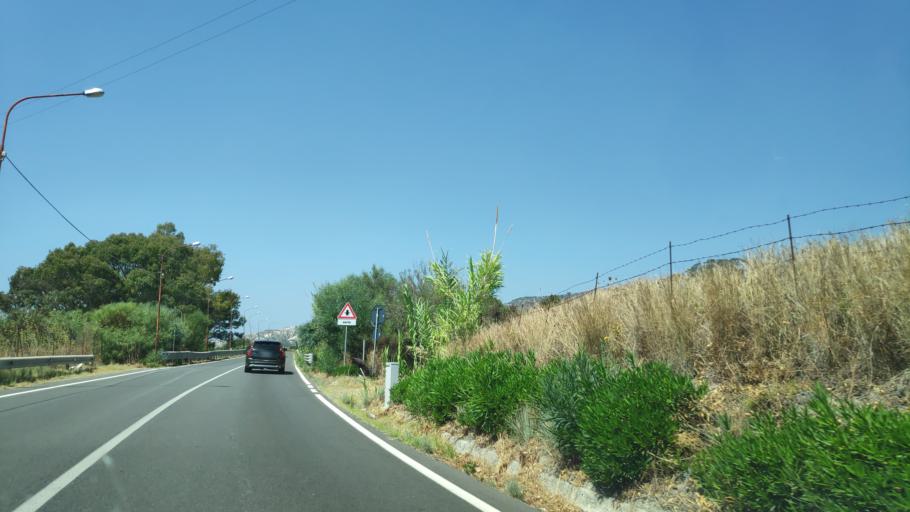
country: IT
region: Calabria
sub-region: Provincia di Reggio Calabria
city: Palizzi Marina
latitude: 37.9241
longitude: 16.0317
